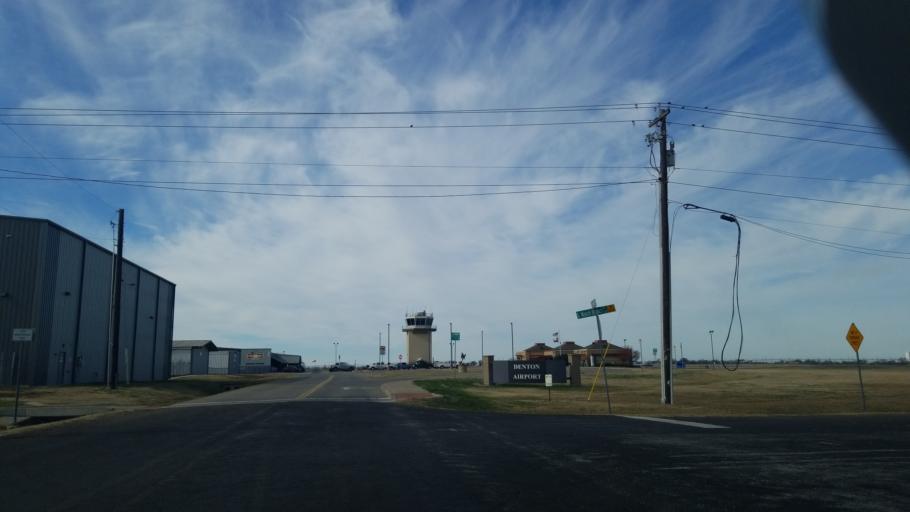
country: US
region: Texas
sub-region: Denton County
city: Denton
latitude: 33.2020
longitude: -97.1925
